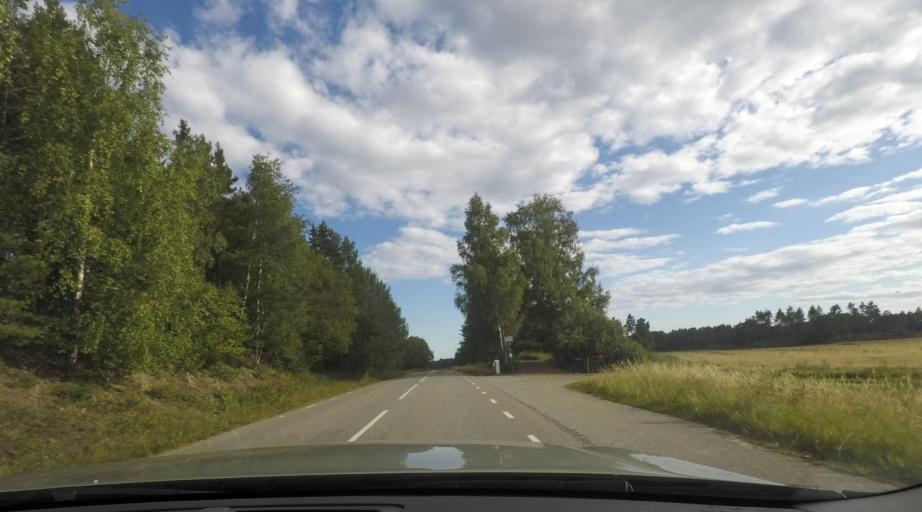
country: SE
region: Soedermanland
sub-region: Trosa Kommun
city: Trosa
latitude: 58.9767
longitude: 17.6930
